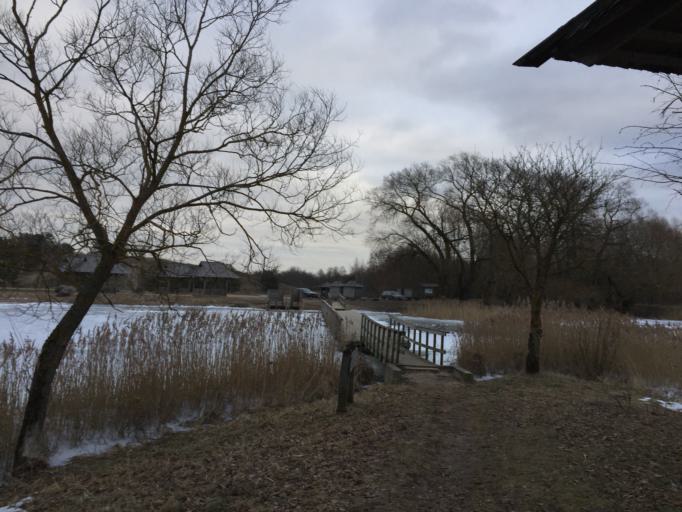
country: LT
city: Zagare
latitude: 56.3534
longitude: 23.2227
